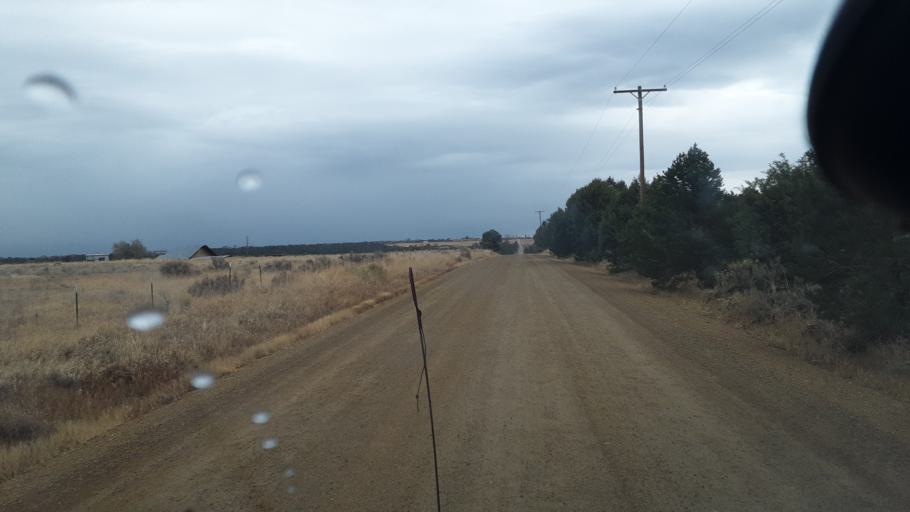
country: US
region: Colorado
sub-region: Montezuma County
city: Mancos
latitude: 37.1986
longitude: -108.1300
